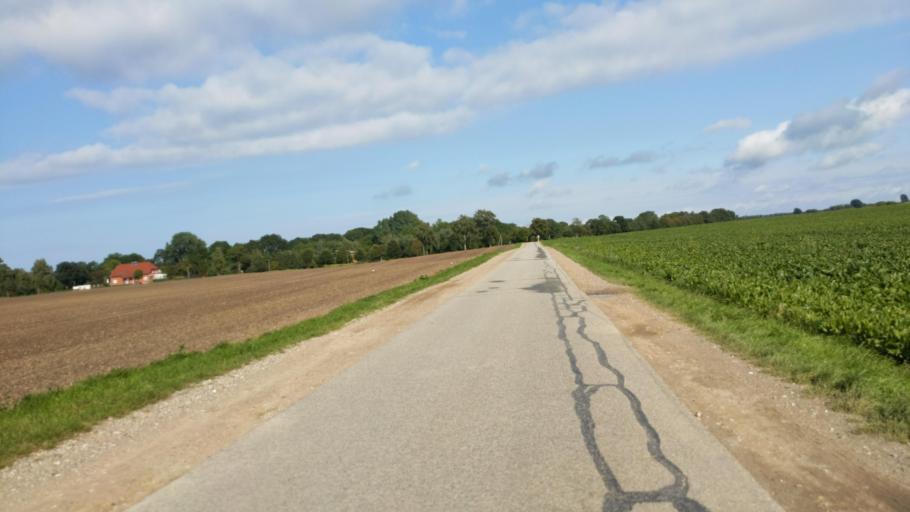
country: DE
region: Mecklenburg-Vorpommern
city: Dassow
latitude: 53.9599
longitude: 10.9831
